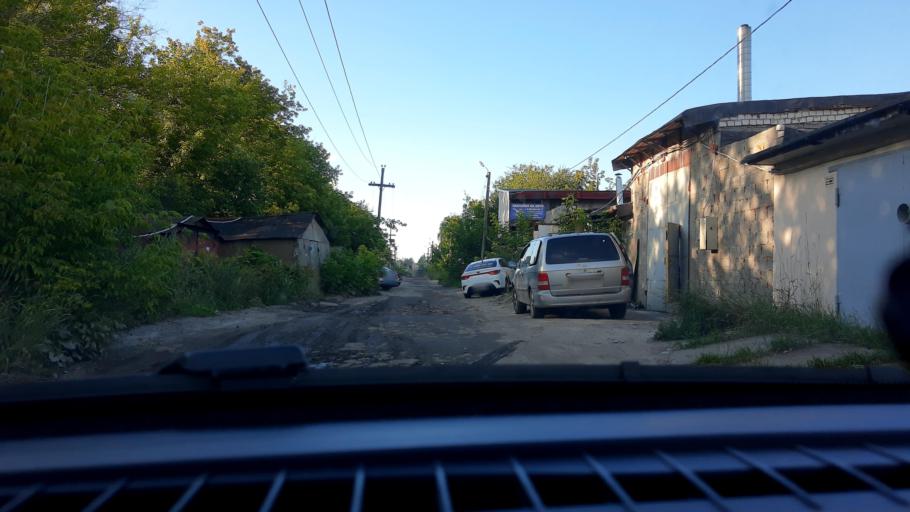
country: RU
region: Nizjnij Novgorod
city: Gorbatovka
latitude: 56.2499
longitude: 43.8243
